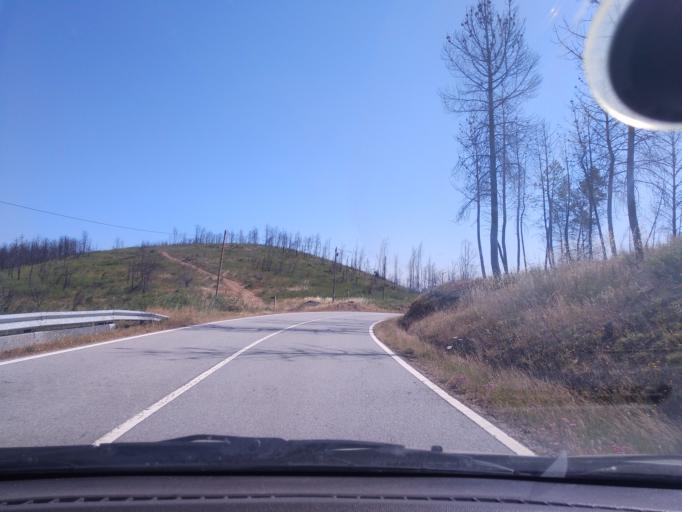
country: PT
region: Portalegre
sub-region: Nisa
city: Nisa
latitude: 39.6244
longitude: -7.6647
